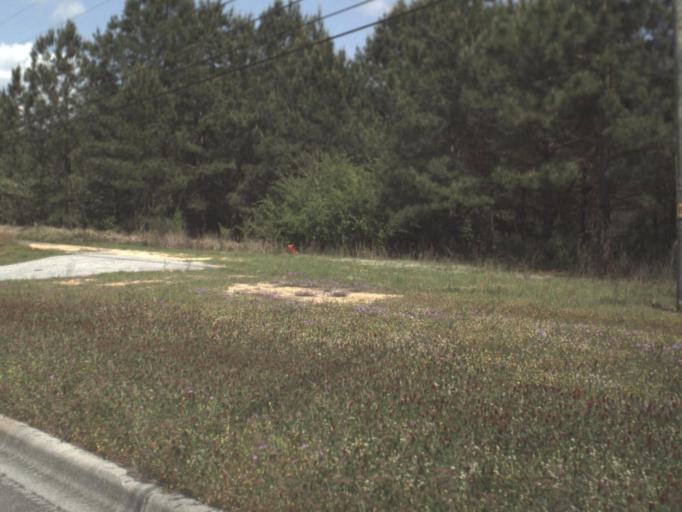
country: US
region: Florida
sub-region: Escambia County
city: Century
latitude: 30.9555
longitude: -87.2788
